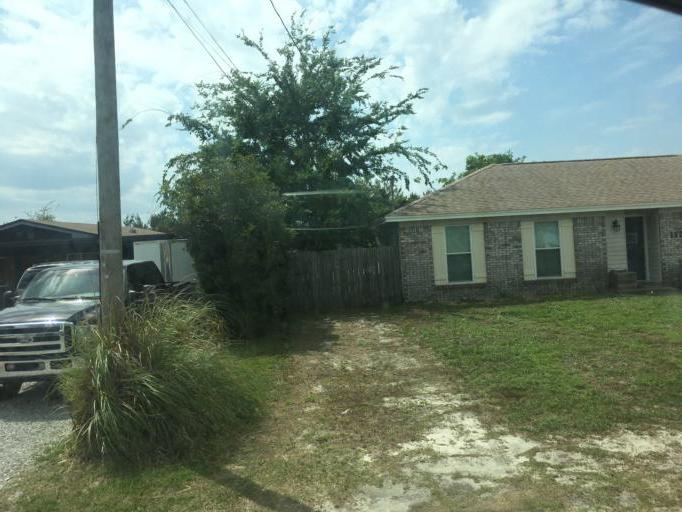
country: US
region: Florida
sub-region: Bay County
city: Laguna Beach
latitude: 30.2344
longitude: -85.8947
